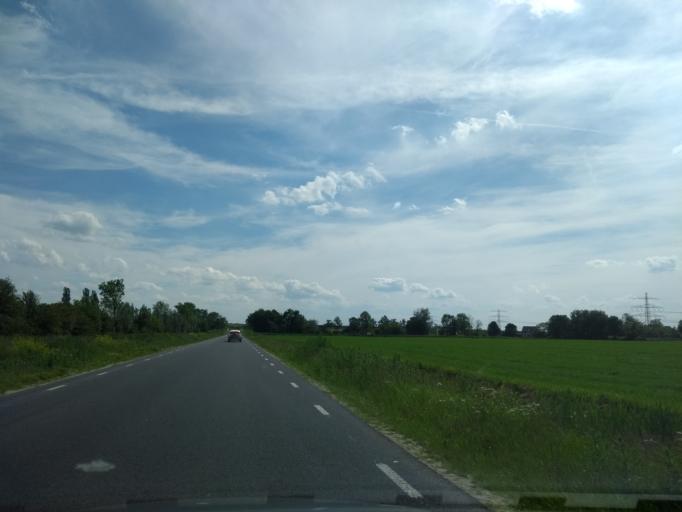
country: NL
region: Groningen
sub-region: Gemeente Zuidhorn
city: Aduard
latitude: 53.2495
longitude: 6.4801
